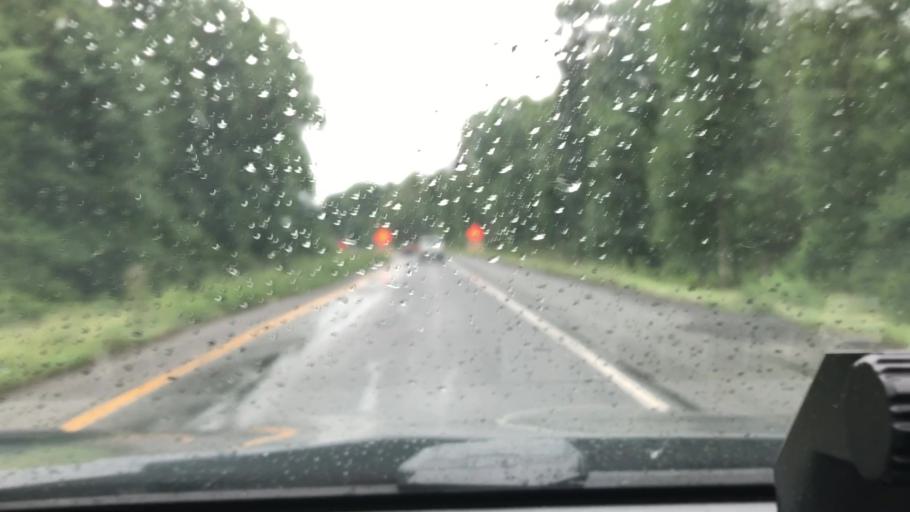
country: US
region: Pennsylvania
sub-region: Monroe County
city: Tannersville
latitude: 40.9984
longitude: -75.2729
